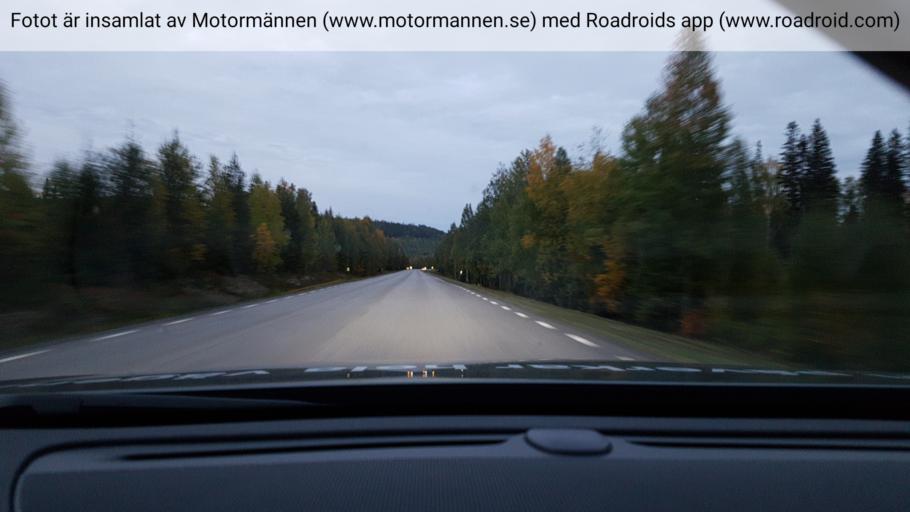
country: SE
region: Norrbotten
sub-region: Alvsbyns Kommun
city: AElvsbyn
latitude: 65.7817
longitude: 20.7850
